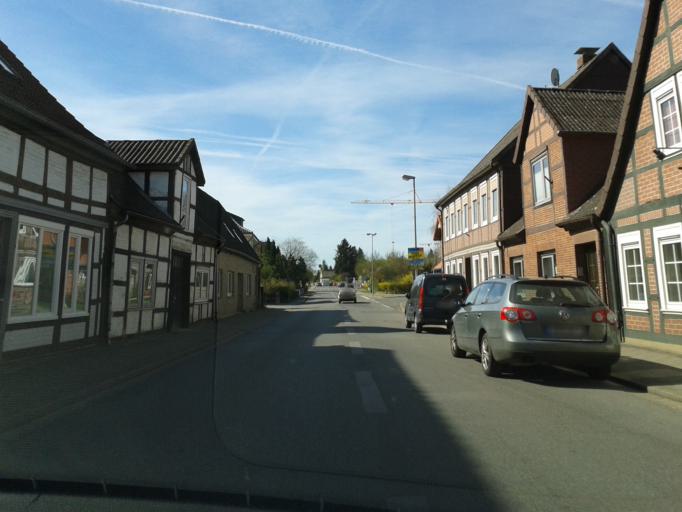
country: DE
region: Lower Saxony
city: Clenze
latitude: 52.9320
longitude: 10.9528
